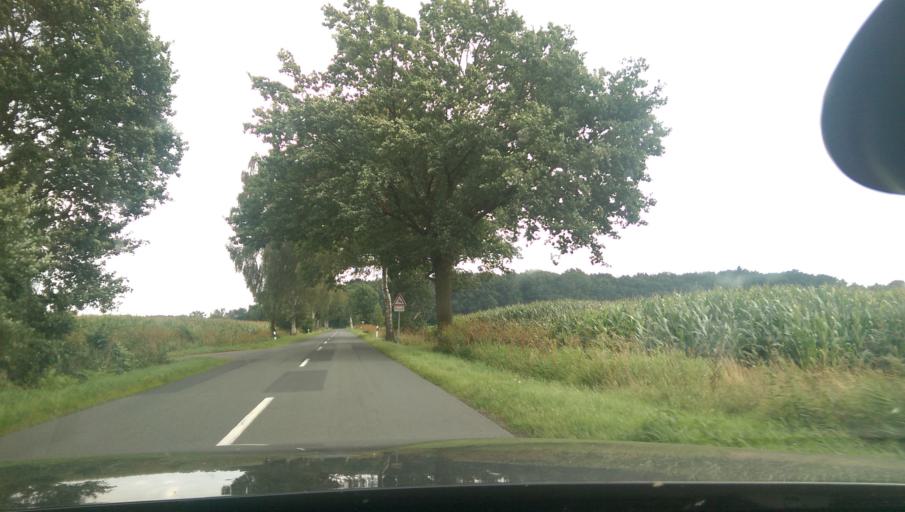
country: DE
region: Lower Saxony
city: Frankenfeld
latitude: 52.7121
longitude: 9.4336
